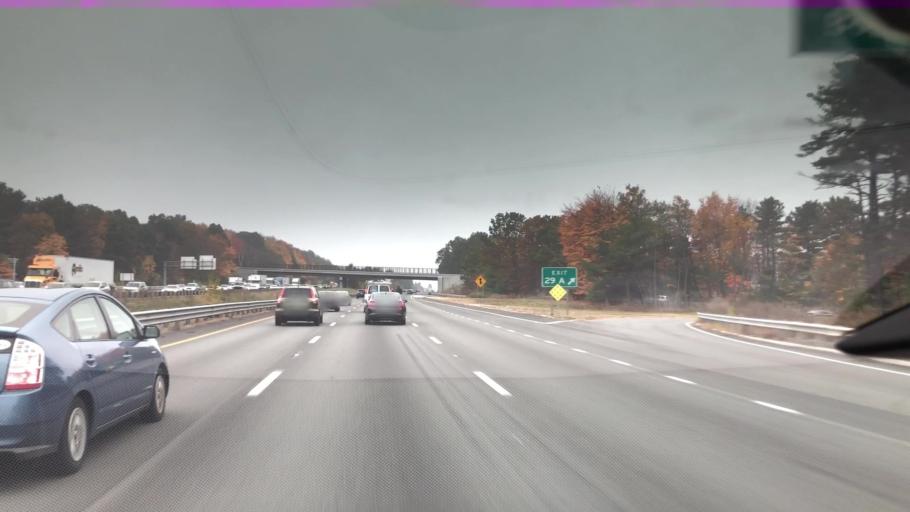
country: US
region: Massachusetts
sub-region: Middlesex County
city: Littleton Common
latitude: 42.5201
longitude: -71.5091
